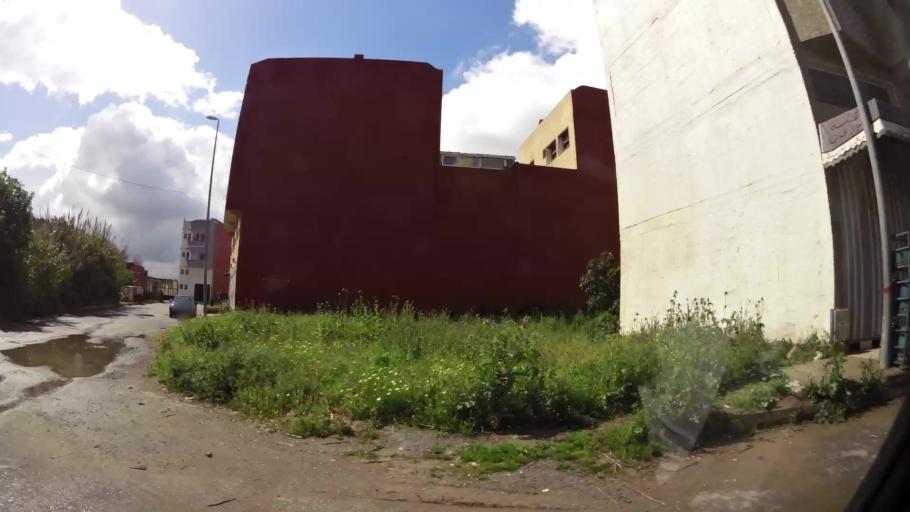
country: MA
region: Grand Casablanca
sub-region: Mediouna
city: Tit Mellil
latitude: 33.5455
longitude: -7.4901
